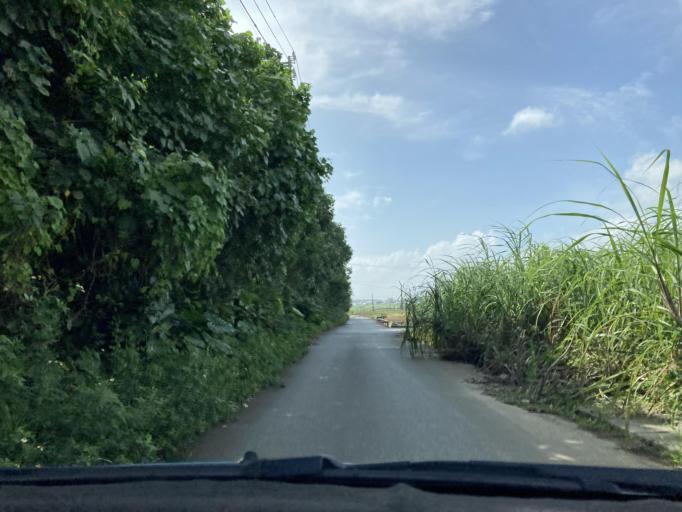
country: JP
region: Okinawa
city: Itoman
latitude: 26.0913
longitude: 127.7068
